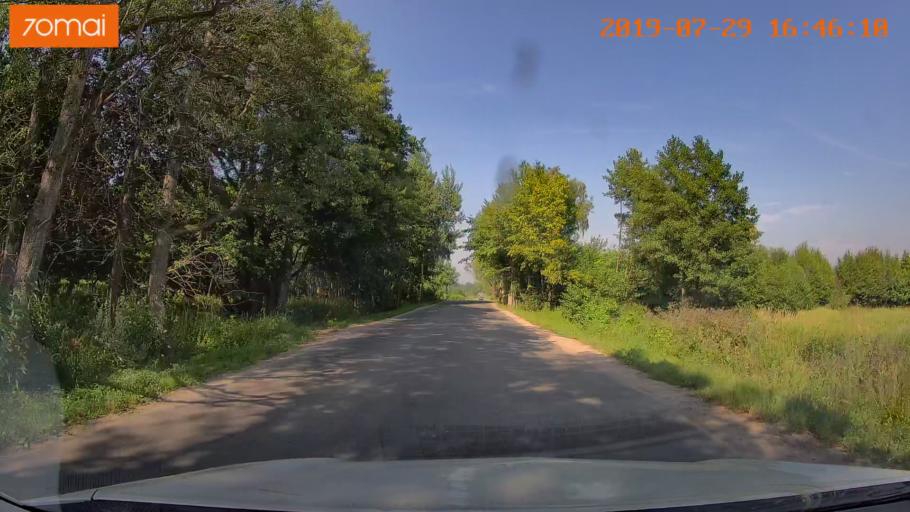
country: RU
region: Kaliningrad
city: Primorsk
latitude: 54.7716
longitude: 20.0817
